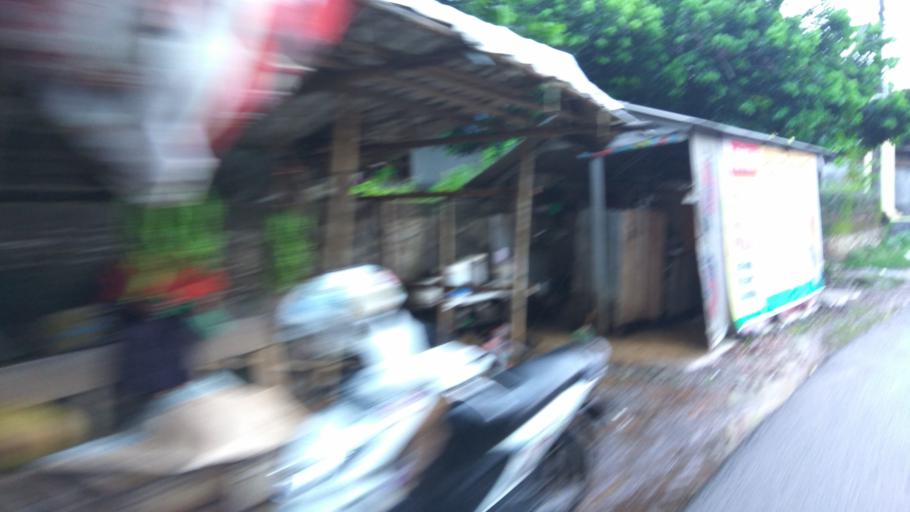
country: ID
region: Central Java
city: Ungaran
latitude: -7.0674
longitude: 110.3974
